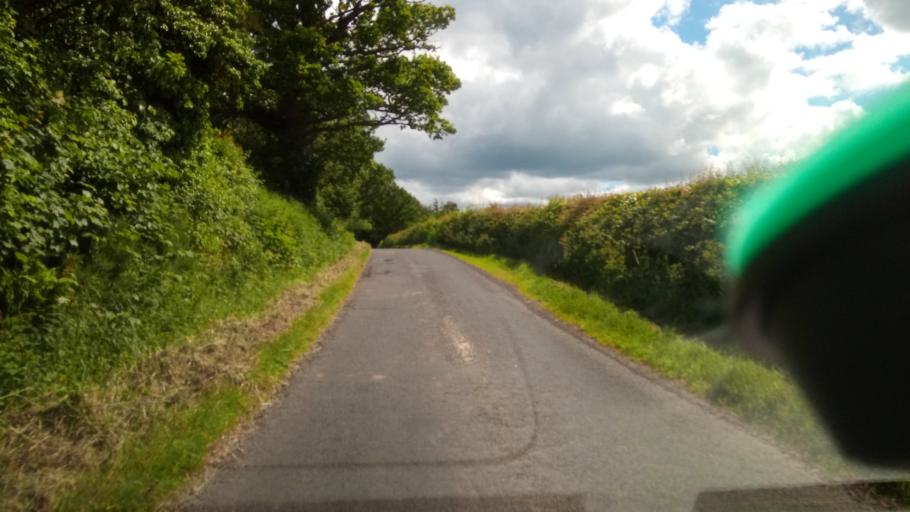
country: GB
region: Scotland
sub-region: The Scottish Borders
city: Jedburgh
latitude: 55.4622
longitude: -2.5476
